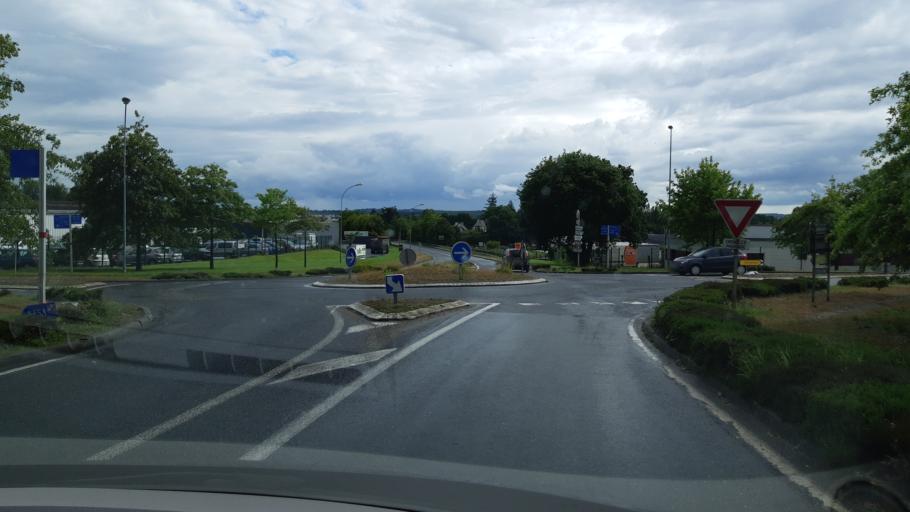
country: FR
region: Brittany
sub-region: Departement du Finistere
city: Landivisiau
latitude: 48.5208
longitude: -4.0707
